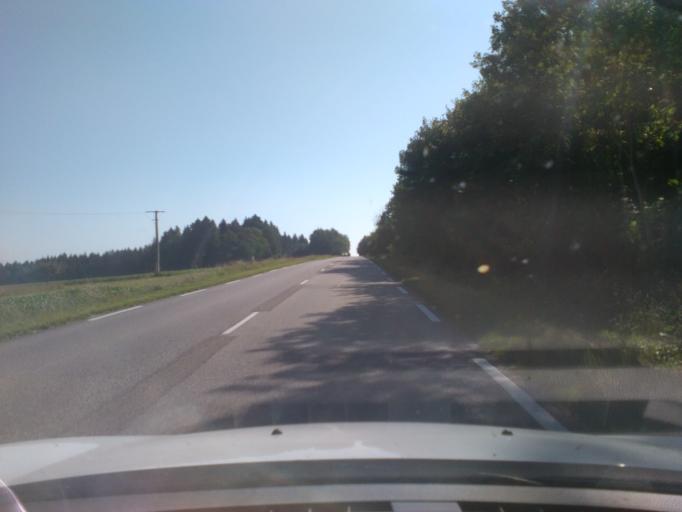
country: FR
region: Lorraine
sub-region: Departement des Vosges
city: Deyvillers
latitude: 48.2037
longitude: 6.5372
